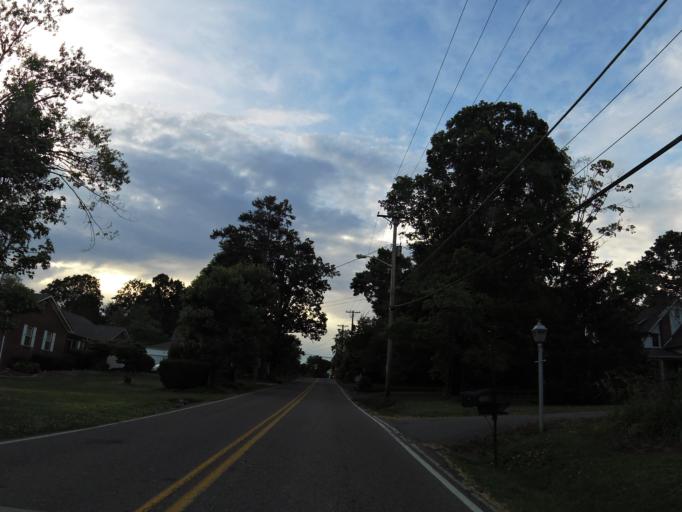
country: US
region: Tennessee
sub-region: Knox County
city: Knoxville
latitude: 36.0395
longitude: -83.9087
